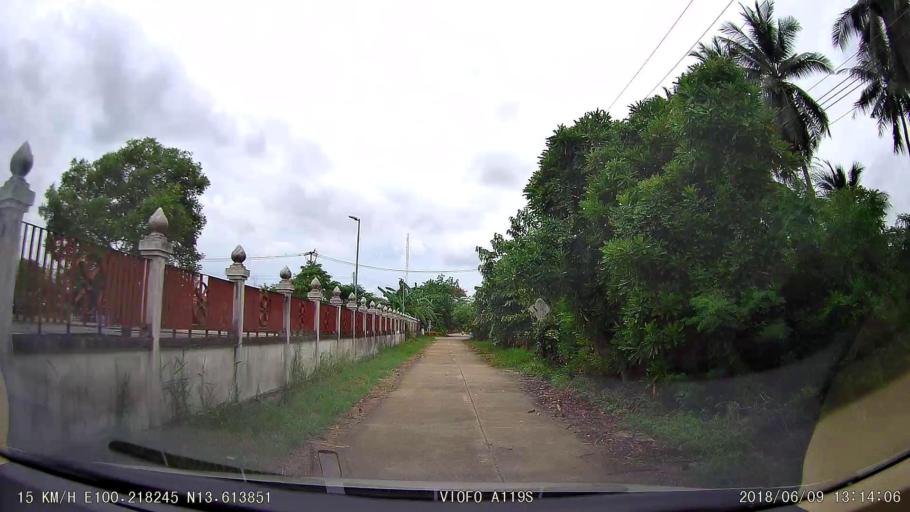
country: TH
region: Samut Sakhon
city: Krathum Baen
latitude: 13.6138
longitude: 100.2182
